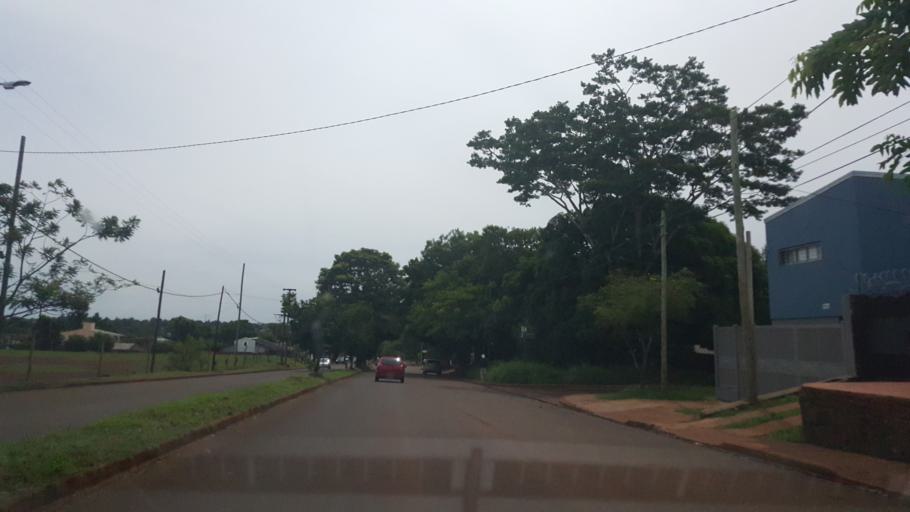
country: AR
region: Misiones
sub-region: Departamento de Capital
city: Posadas
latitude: -27.3944
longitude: -55.9431
